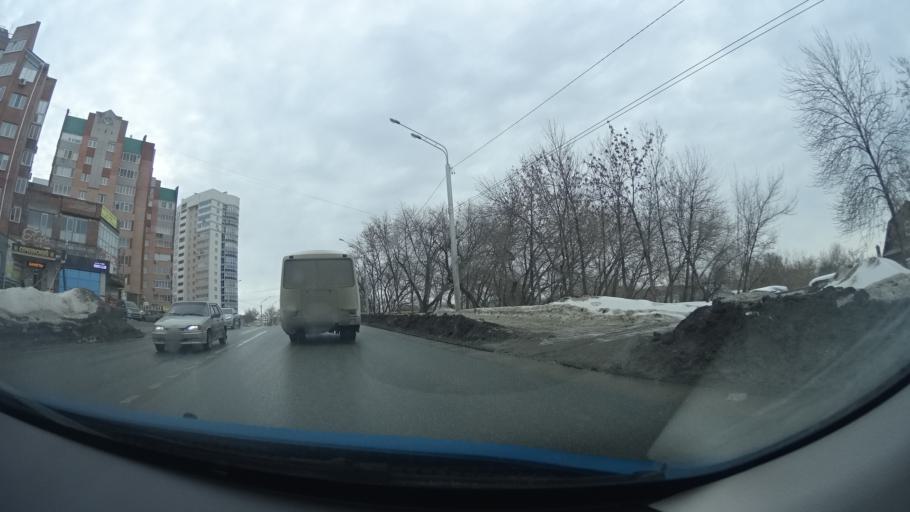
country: RU
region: Bashkortostan
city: Ufa
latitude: 54.7033
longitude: 55.9765
